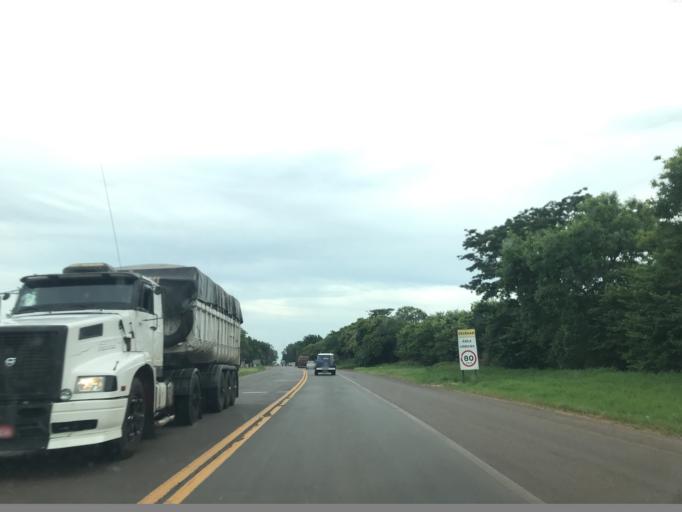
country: BR
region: Sao Paulo
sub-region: Tupa
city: Tupa
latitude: -21.6397
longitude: -50.4966
